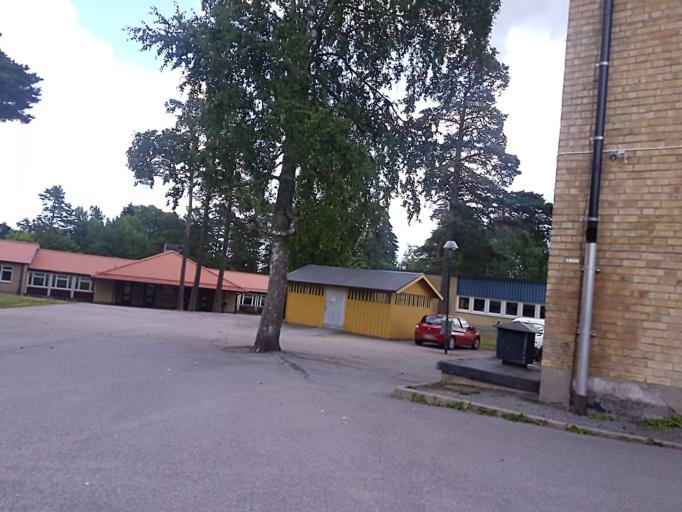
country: SE
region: Soedermanland
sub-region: Gnesta Kommun
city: Gnesta
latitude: 59.0451
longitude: 17.3173
